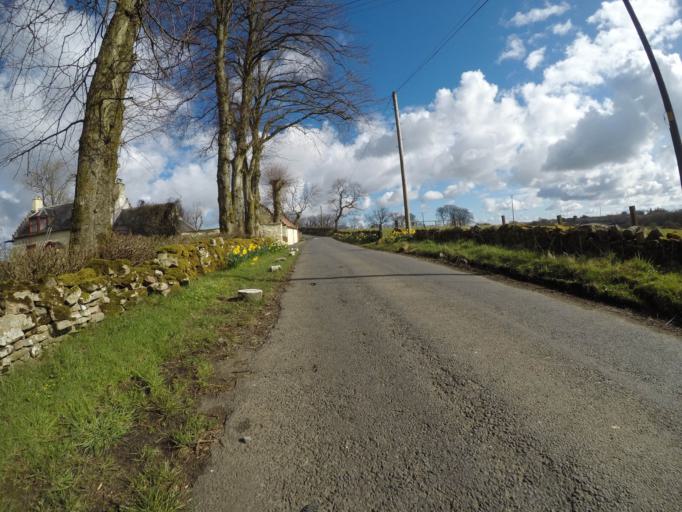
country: GB
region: Scotland
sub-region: North Ayrshire
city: Beith
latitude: 55.7198
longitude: -4.6187
